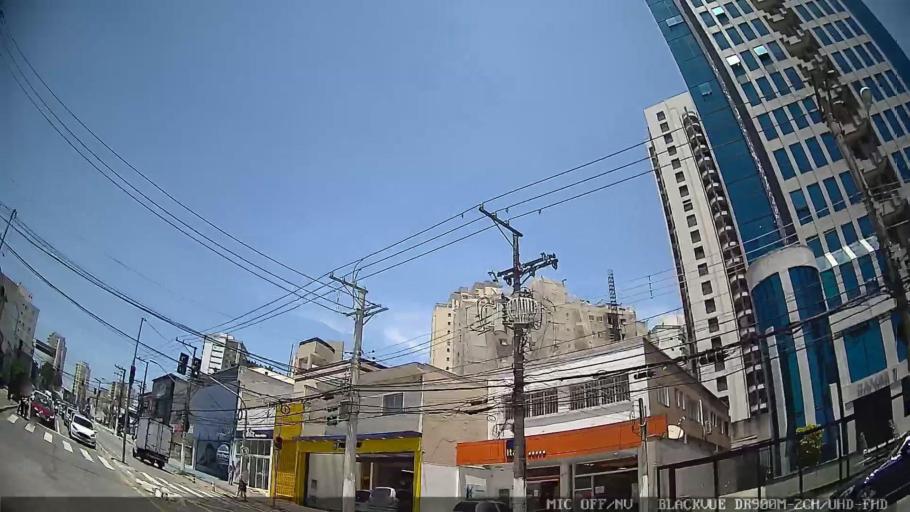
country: BR
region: Sao Paulo
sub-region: Sao Caetano Do Sul
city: Sao Caetano do Sul
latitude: -23.5530
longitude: -46.5647
